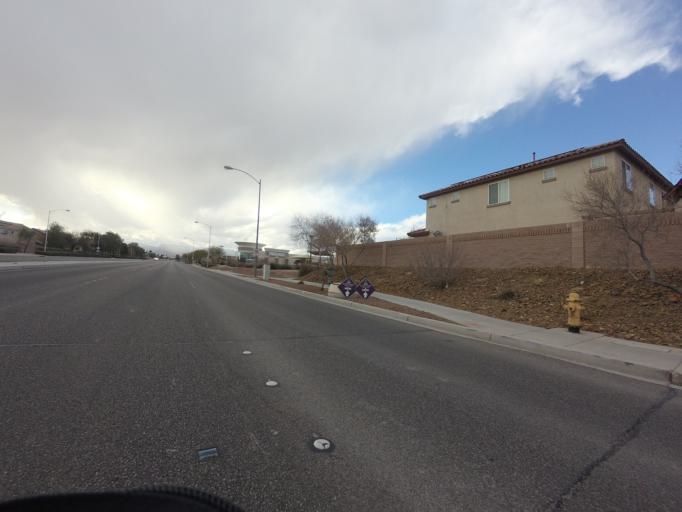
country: US
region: Nevada
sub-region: Clark County
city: North Las Vegas
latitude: 36.2618
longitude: -115.1848
